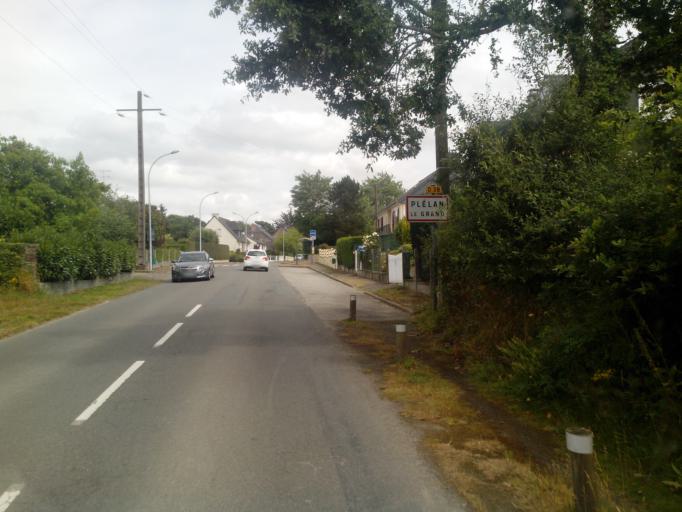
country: FR
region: Brittany
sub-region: Departement d'Ille-et-Vilaine
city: Plelan-le-Grand
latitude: 48.0008
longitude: -2.1084
